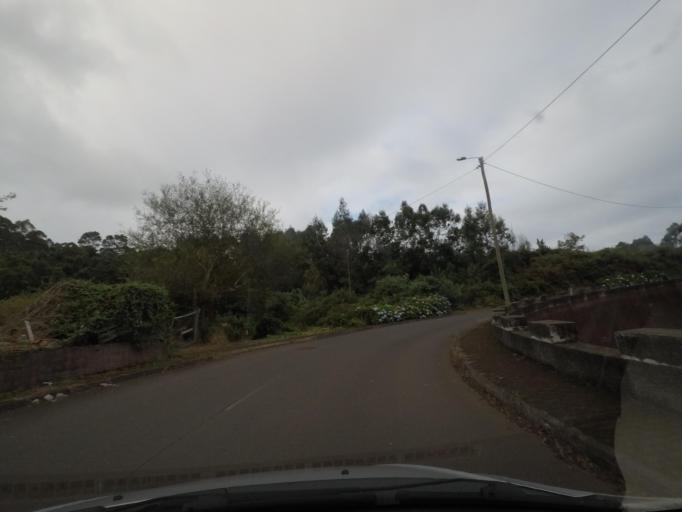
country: PT
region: Madeira
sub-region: Santana
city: Santana
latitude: 32.7848
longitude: -16.8792
